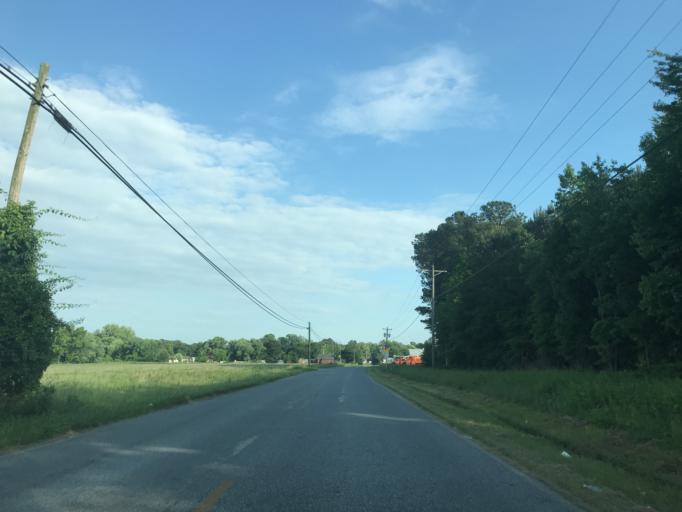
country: US
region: Maryland
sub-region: Caroline County
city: Federalsburg
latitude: 38.7172
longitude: -75.7798
